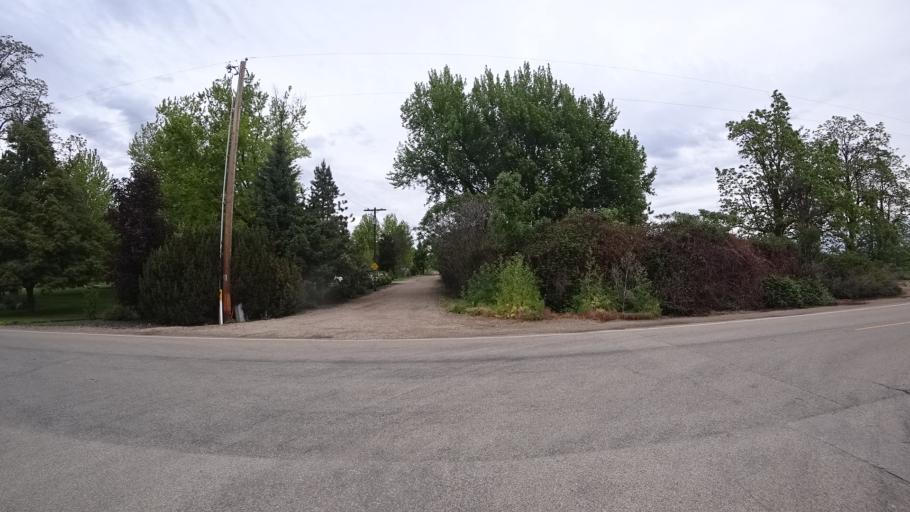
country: US
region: Idaho
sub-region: Ada County
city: Star
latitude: 43.7176
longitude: -116.5029
